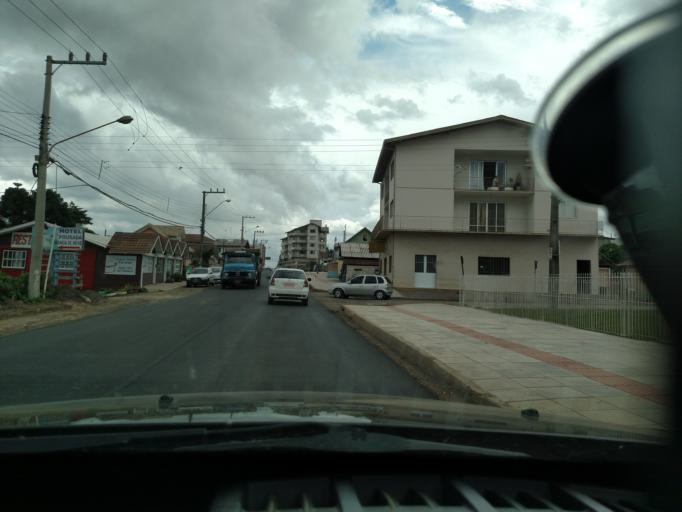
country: BR
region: Santa Catarina
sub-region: Sao Joaquim
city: Sao Joaquim
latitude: -28.2854
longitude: -49.9325
